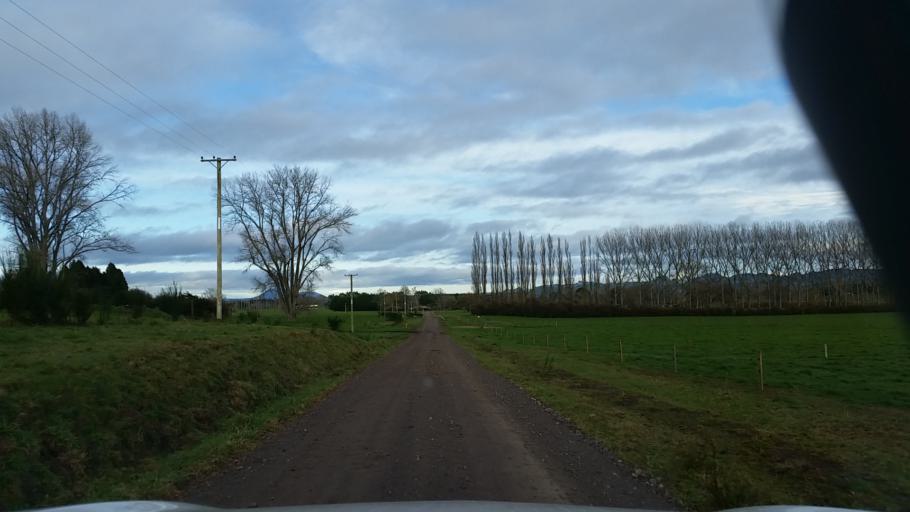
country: NZ
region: Bay of Plenty
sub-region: Rotorua District
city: Rotorua
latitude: -38.3924
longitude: 176.3929
